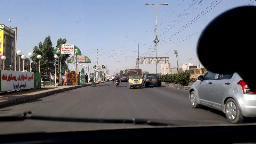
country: PK
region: Sindh
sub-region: Karachi District
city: Karachi
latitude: 24.9009
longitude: 67.1135
